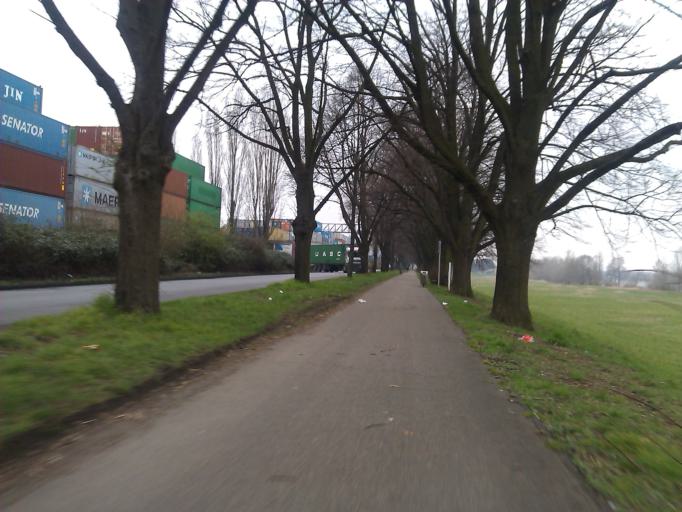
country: DE
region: North Rhine-Westphalia
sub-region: Regierungsbezirk Koln
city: Riehl
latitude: 50.9802
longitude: 6.9823
